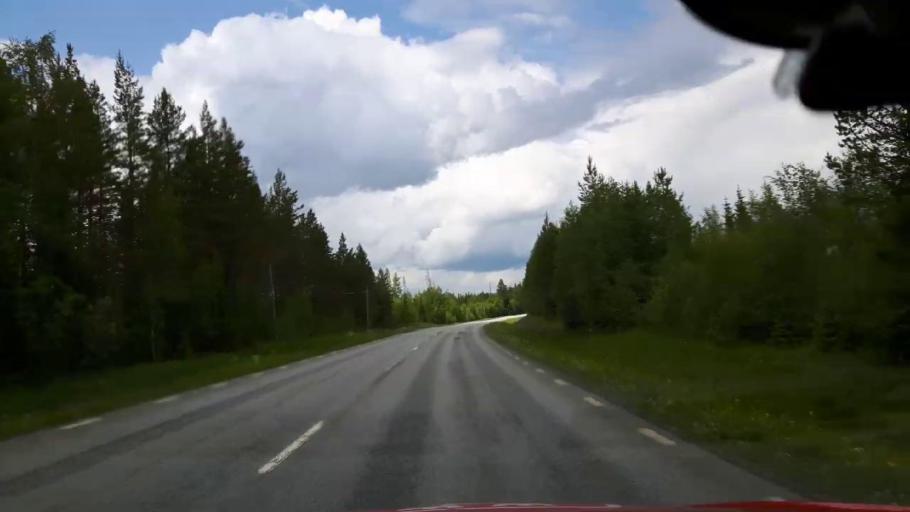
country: SE
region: Jaemtland
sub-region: Krokoms Kommun
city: Krokom
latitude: 63.3592
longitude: 14.4044
